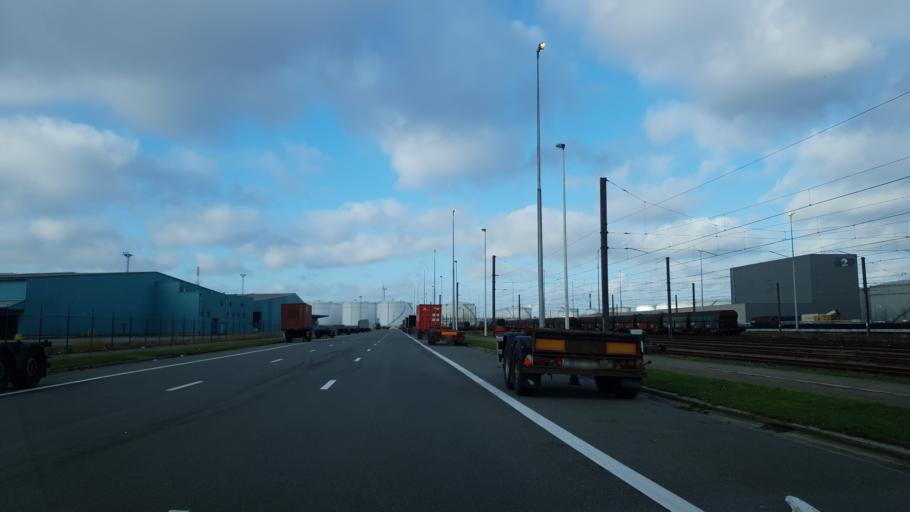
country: BE
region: Flanders
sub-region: Provincie Antwerpen
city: Zwijndrecht
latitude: 51.2662
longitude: 4.3562
